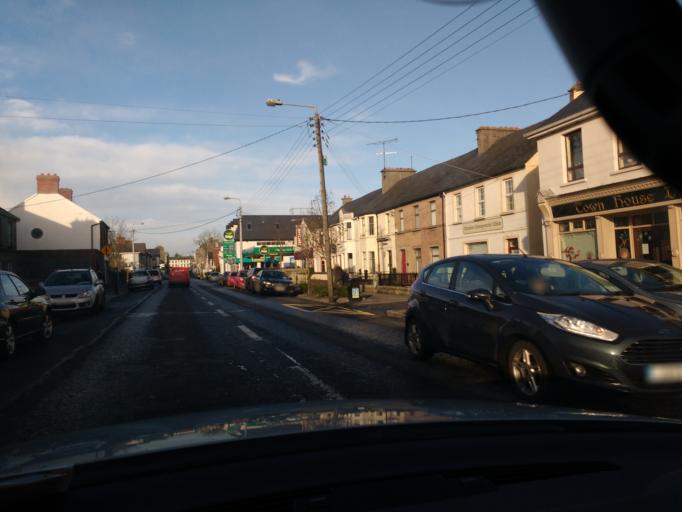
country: IE
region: Munster
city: Thurles
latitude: 52.6761
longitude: -7.8123
